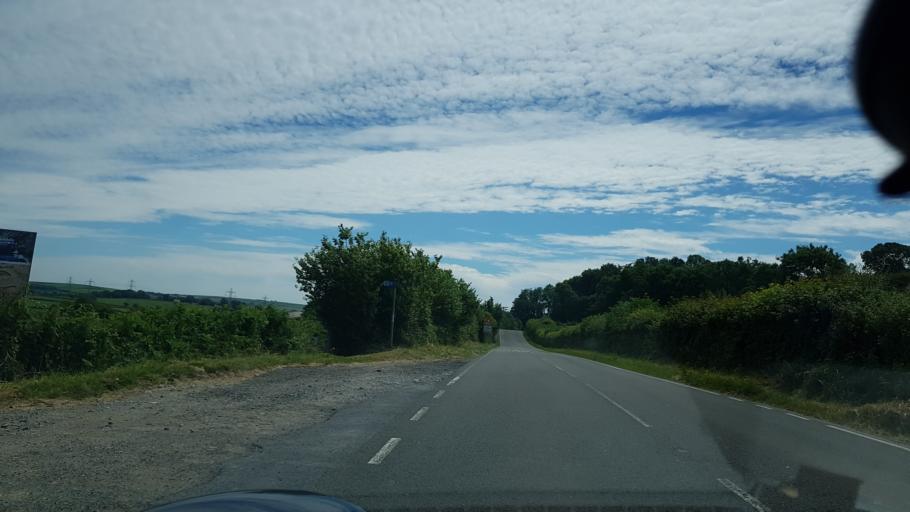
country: GB
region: Wales
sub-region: Carmarthenshire
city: Saint Clears
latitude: 51.8020
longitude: -4.4935
